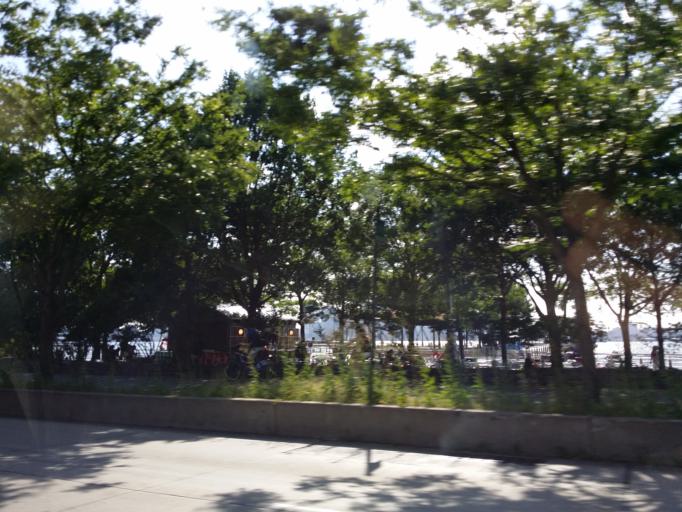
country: US
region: New York
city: New York City
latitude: 40.7334
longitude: -74.0103
